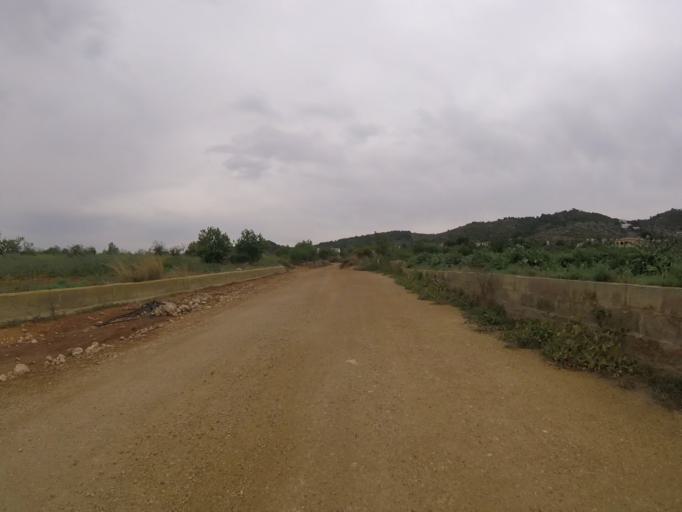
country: ES
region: Valencia
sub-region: Provincia de Castello
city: Alcoceber
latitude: 40.2452
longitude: 0.2587
